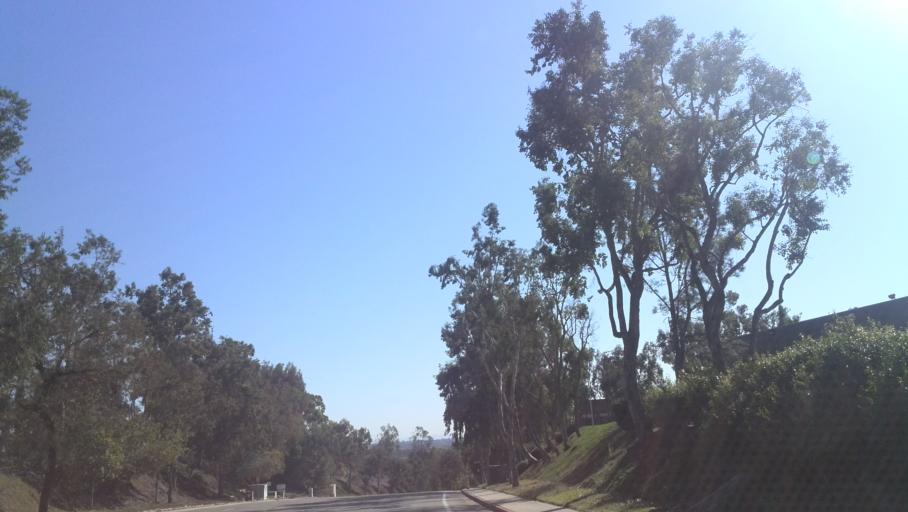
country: US
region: California
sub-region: San Diego County
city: San Diego
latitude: 32.8132
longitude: -117.1209
